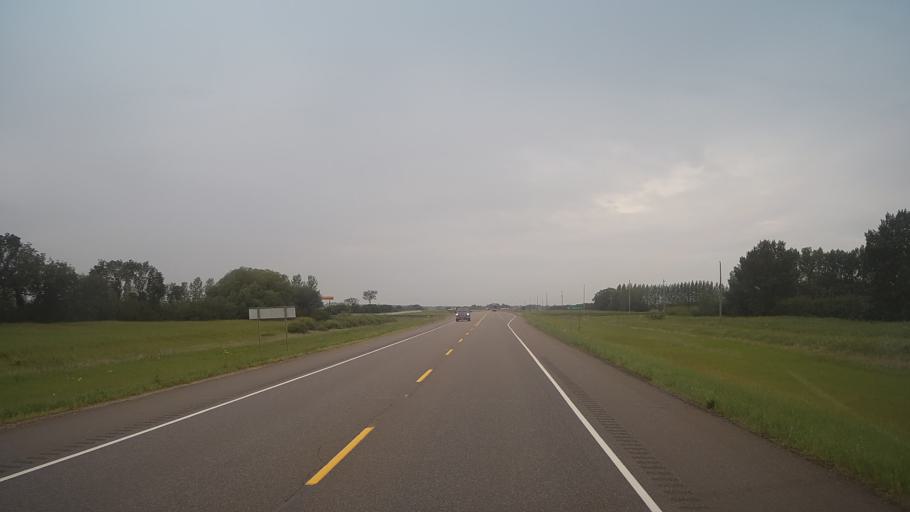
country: CA
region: Saskatchewan
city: Dalmeny
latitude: 52.1293
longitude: -106.8801
